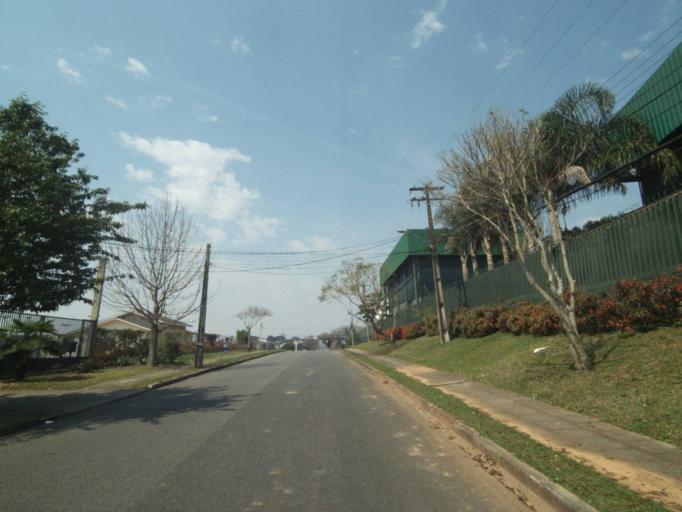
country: BR
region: Parana
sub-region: Curitiba
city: Curitiba
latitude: -25.4590
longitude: -49.2653
